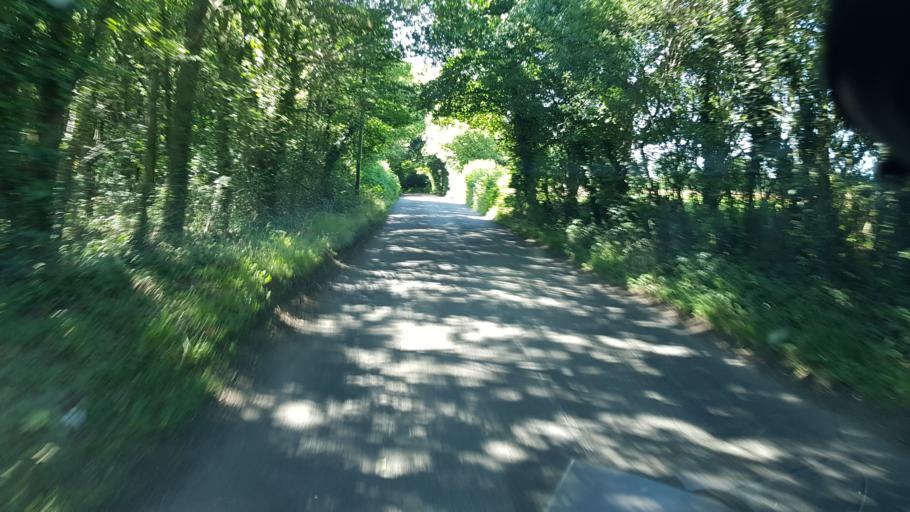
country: GB
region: England
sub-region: Kent
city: Edenbridge
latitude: 51.2203
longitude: 0.0919
